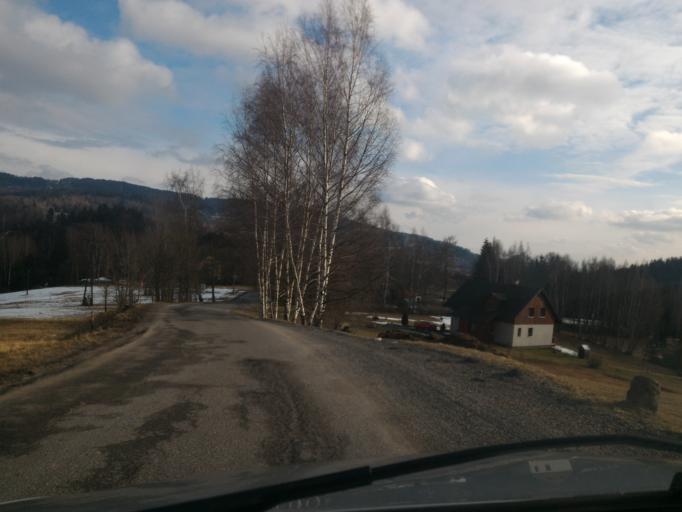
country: CZ
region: Liberecky
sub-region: Okres Jablonec nad Nisou
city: Desna
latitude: 50.7534
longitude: 15.2994
